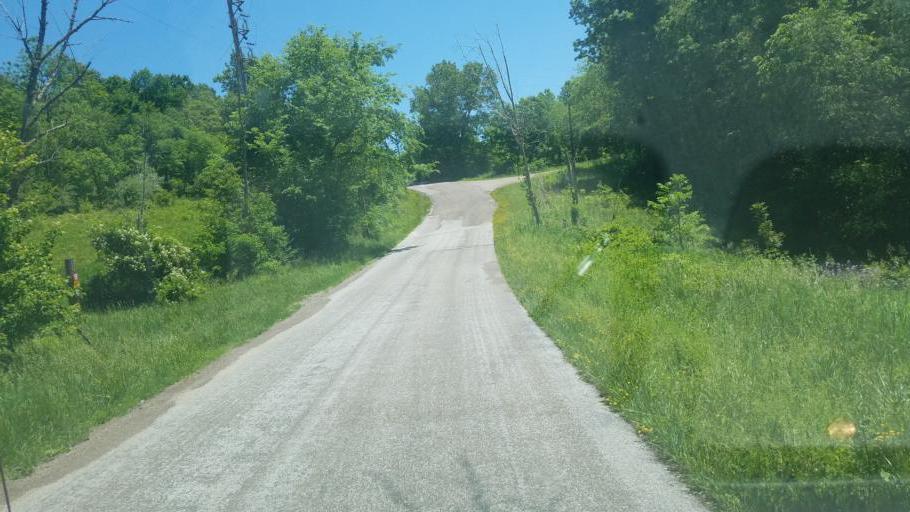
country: US
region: Ohio
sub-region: Coshocton County
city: Coshocton
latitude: 40.2682
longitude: -81.9610
